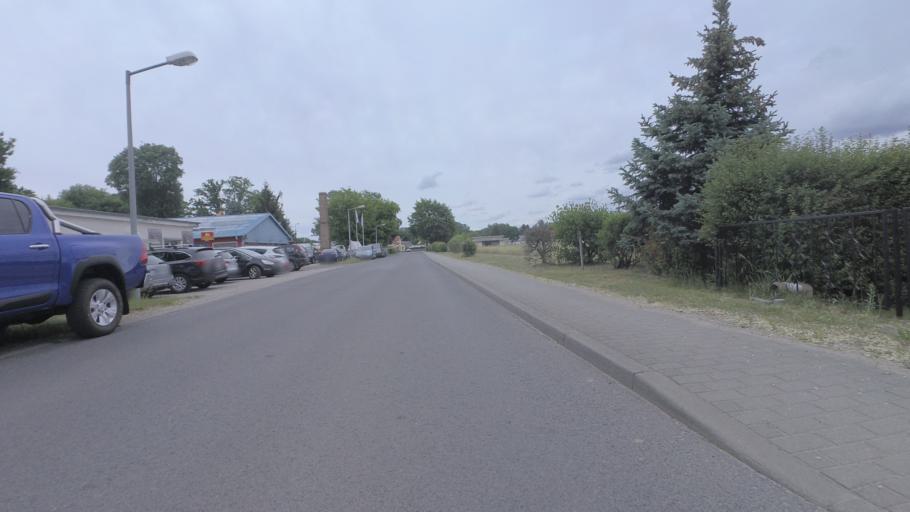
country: DE
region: Brandenburg
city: Bestensee
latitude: 52.2807
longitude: 13.7431
